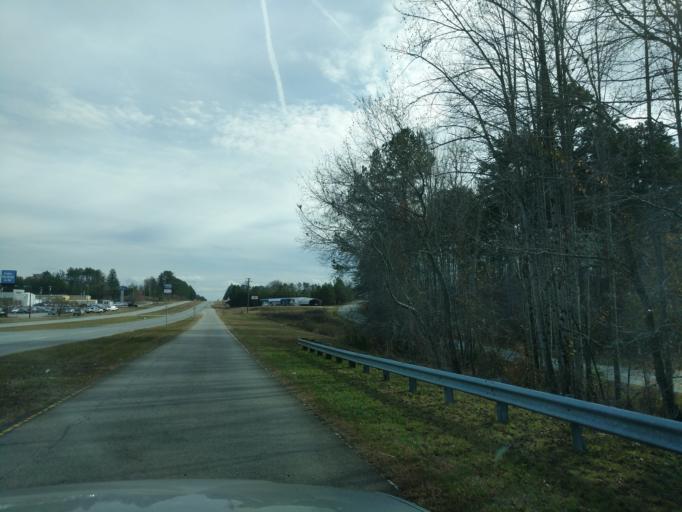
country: US
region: South Carolina
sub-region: Oconee County
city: Walhalla
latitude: 34.7511
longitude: -83.0451
